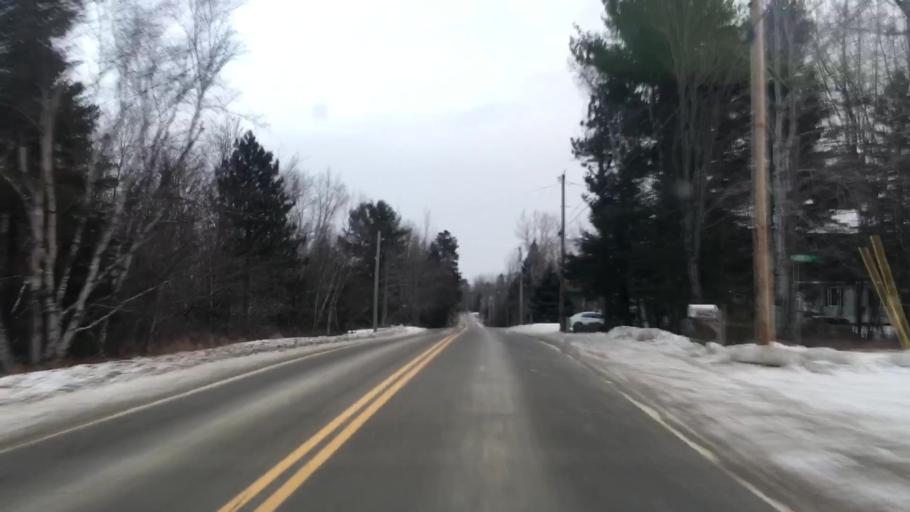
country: US
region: Maine
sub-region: Hancock County
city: Ellsworth
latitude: 44.6047
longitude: -68.3954
